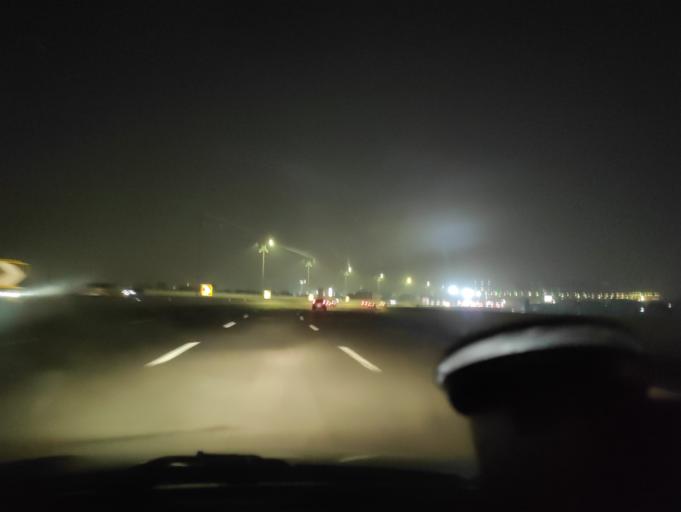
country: EG
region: Muhafazat al Qahirah
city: Cairo
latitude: 30.1124
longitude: 31.2203
